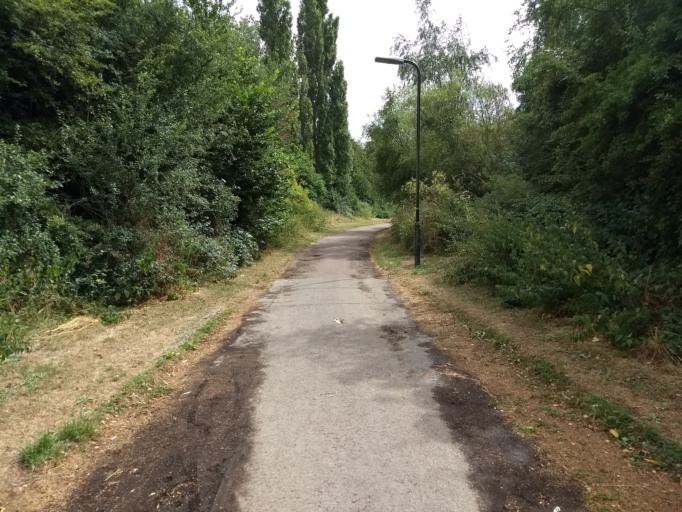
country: GB
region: England
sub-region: Milton Keynes
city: Newport Pagnell
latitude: 52.0723
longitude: -0.7313
